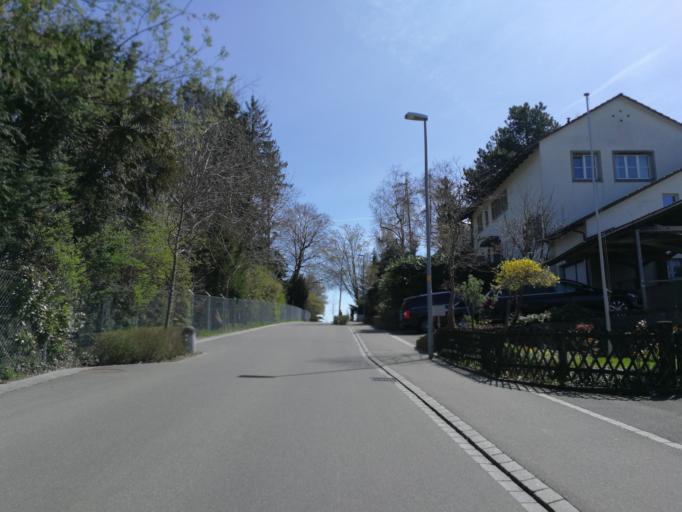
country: CH
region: Zurich
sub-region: Bezirk Meilen
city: Feldmeilen
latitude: 47.2826
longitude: 8.6219
